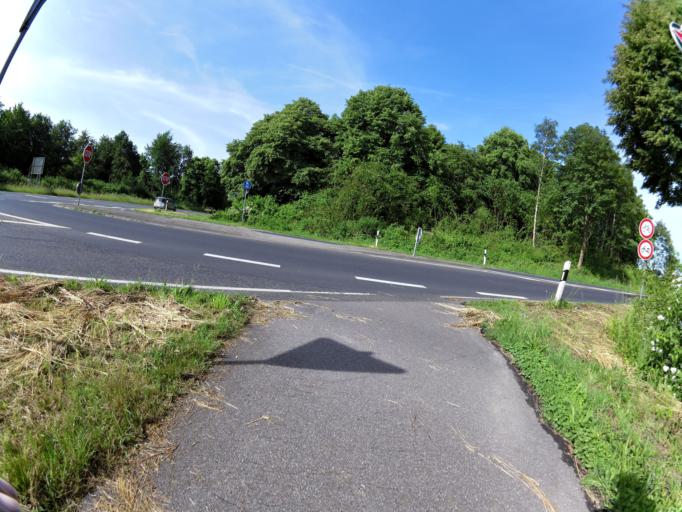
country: DE
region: North Rhine-Westphalia
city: Geilenkirchen
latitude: 50.9583
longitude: 6.1026
